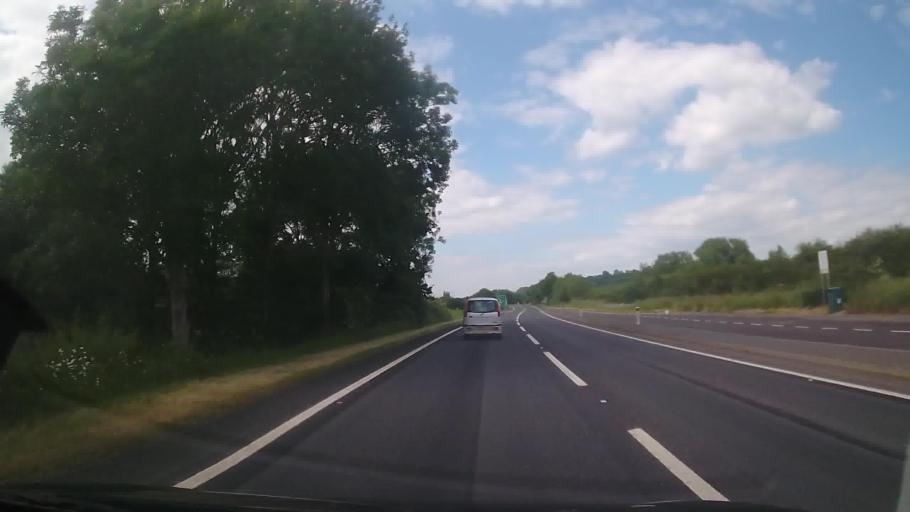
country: GB
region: England
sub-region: Herefordshire
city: Leominster
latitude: 52.2176
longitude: -2.7261
